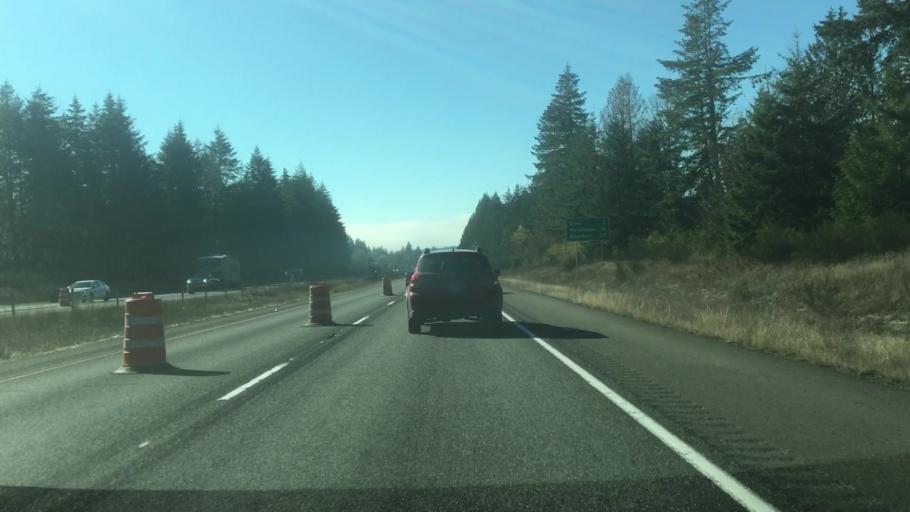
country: US
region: Washington
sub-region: Grays Harbor County
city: McCleary
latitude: 47.0530
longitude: -123.2926
